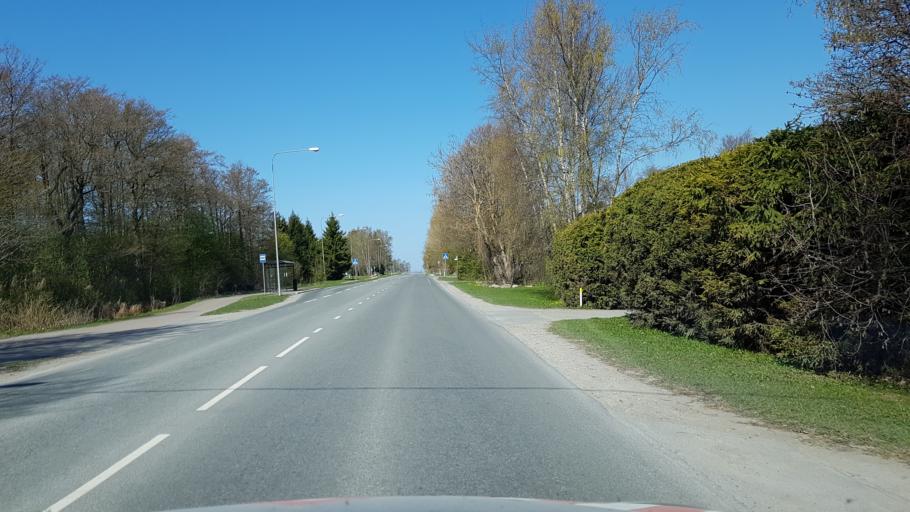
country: EE
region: Harju
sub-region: Viimsi vald
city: Rummu
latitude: 59.5213
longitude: 24.8050
